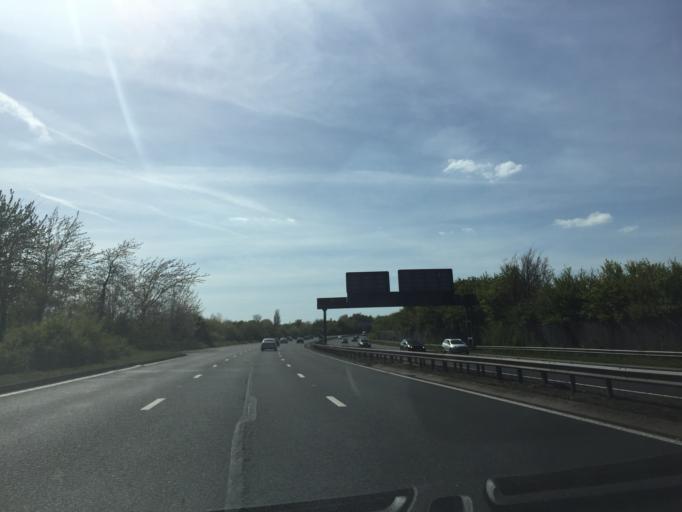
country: GB
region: England
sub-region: Kent
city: Swanley
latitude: 51.3891
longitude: 0.1771
